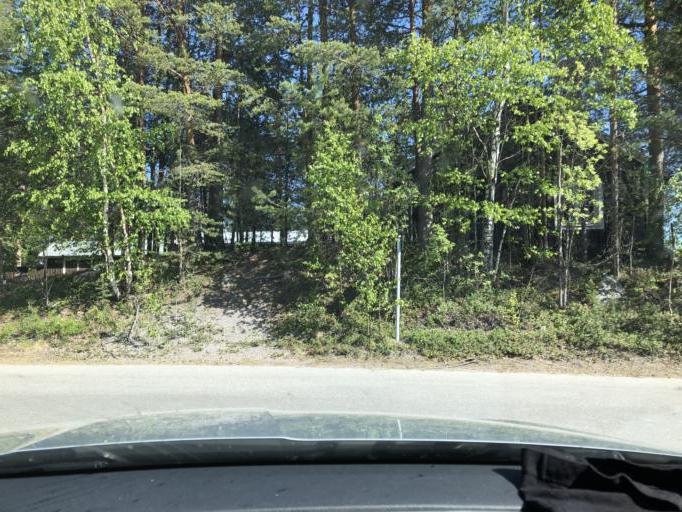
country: SE
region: Norrbotten
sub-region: Jokkmokks Kommun
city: Jokkmokk
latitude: 66.6018
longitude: 19.8459
